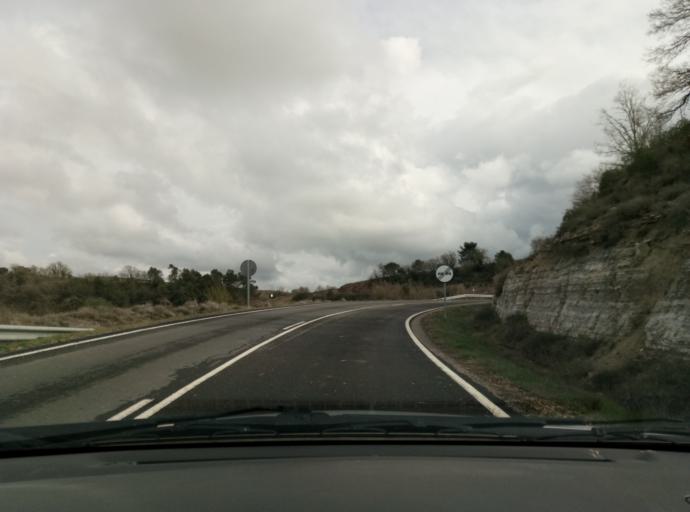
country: ES
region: Catalonia
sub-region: Provincia de Tarragona
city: Santa Coloma de Queralt
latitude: 41.5752
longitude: 1.3371
